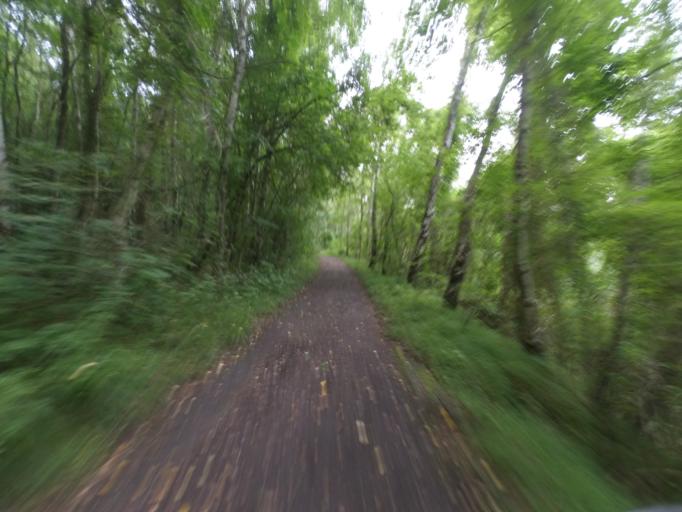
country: DE
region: Schleswig-Holstein
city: Oststeinbek
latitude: 53.5051
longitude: 10.1761
